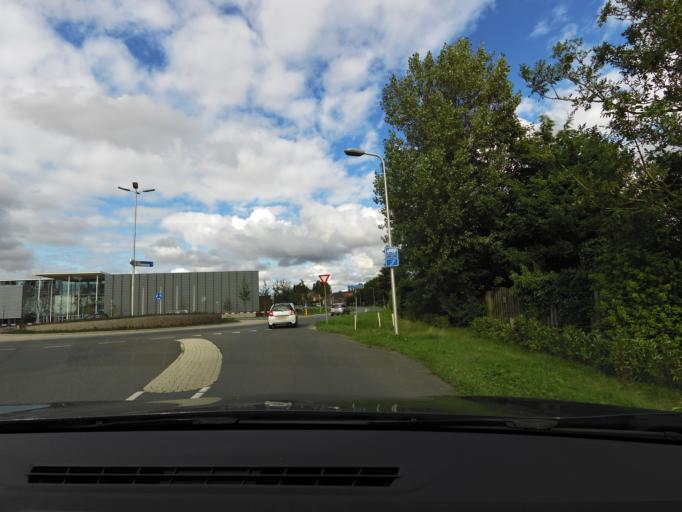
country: NL
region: South Holland
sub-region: Gemeente Brielle
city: Brielle
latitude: 51.8899
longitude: 4.1790
